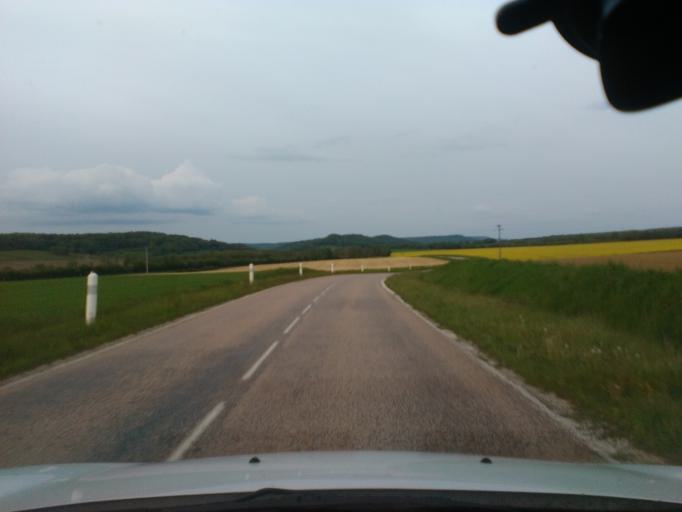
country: FR
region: Champagne-Ardenne
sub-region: Departement de la Haute-Marne
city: Doulaincourt-Saucourt
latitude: 48.2308
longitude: 5.2699
